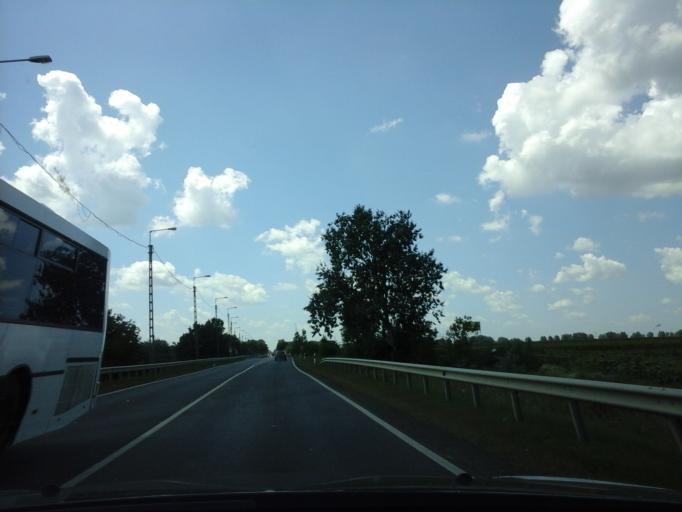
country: HU
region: Hajdu-Bihar
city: Ebes
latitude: 47.4835
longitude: 21.5058
